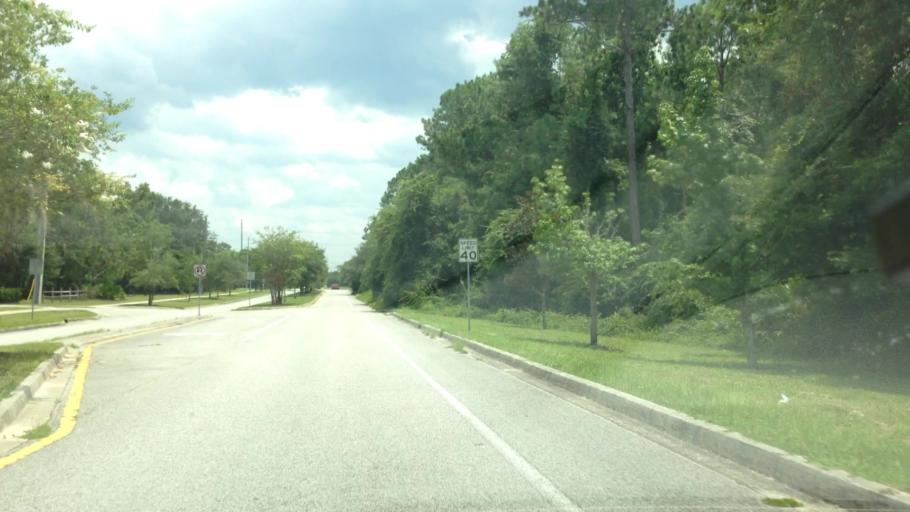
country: US
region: Florida
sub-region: Duval County
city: Neptune Beach
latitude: 30.2994
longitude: -81.5051
